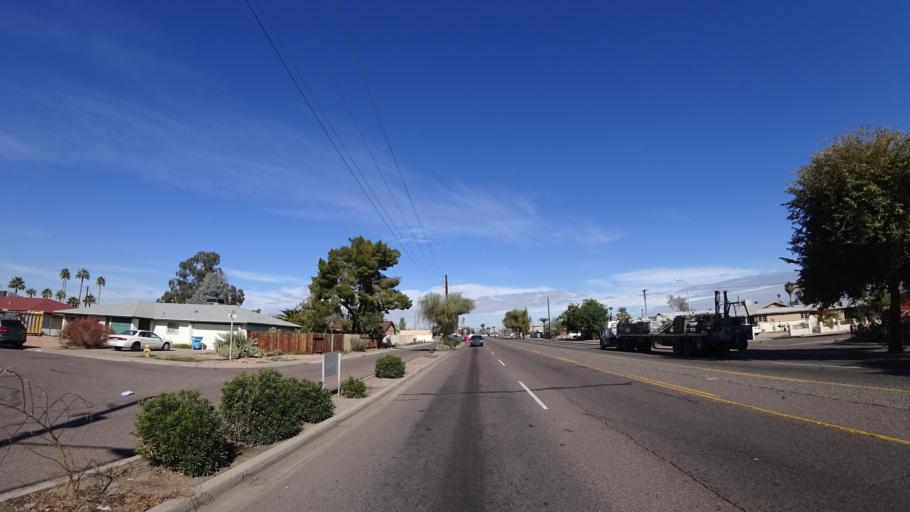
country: US
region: Arizona
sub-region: Maricopa County
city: Glendale
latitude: 33.5070
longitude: -112.1865
